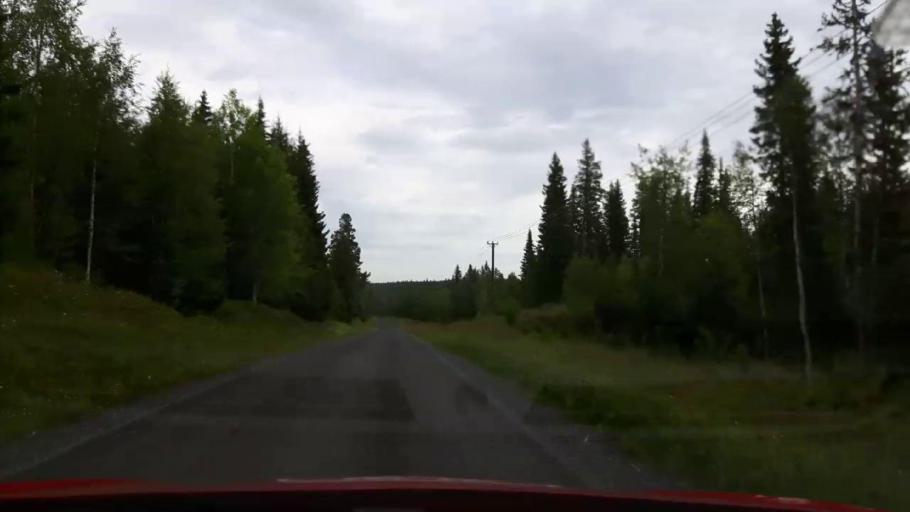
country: SE
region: Jaemtland
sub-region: Stroemsunds Kommun
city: Stroemsund
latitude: 63.4706
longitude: 15.2879
